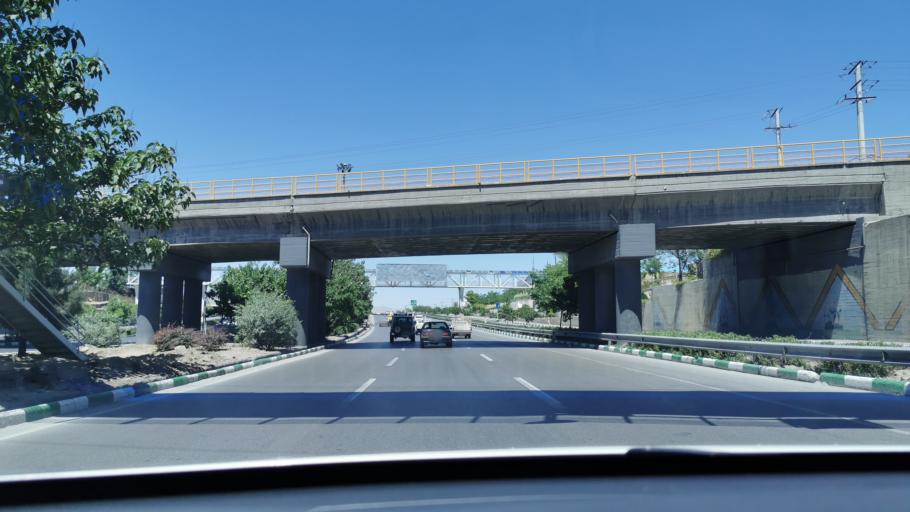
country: IR
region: Razavi Khorasan
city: Mashhad
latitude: 36.2629
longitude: 59.6513
